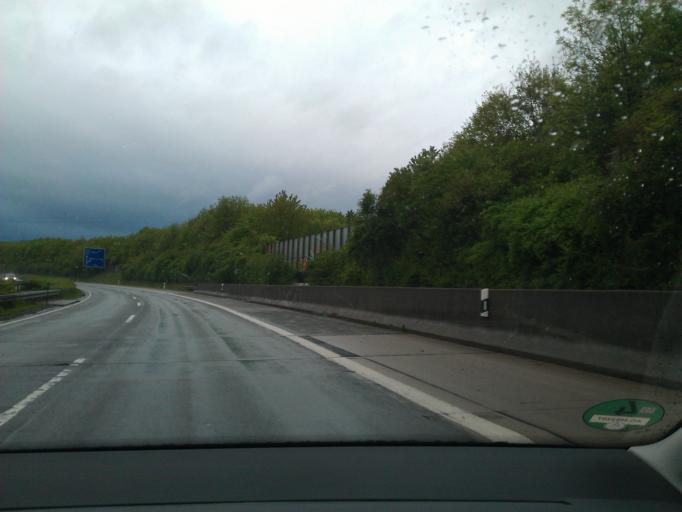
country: DE
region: North Rhine-Westphalia
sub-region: Regierungsbezirk Koln
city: Hennef
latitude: 50.7836
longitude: 7.2824
